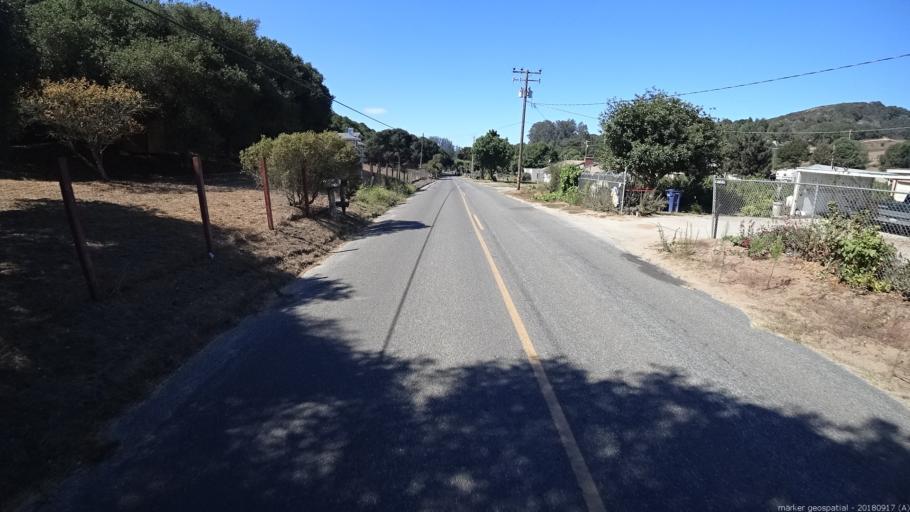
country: US
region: California
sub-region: Monterey County
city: Elkhorn
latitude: 36.8297
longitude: -121.7039
